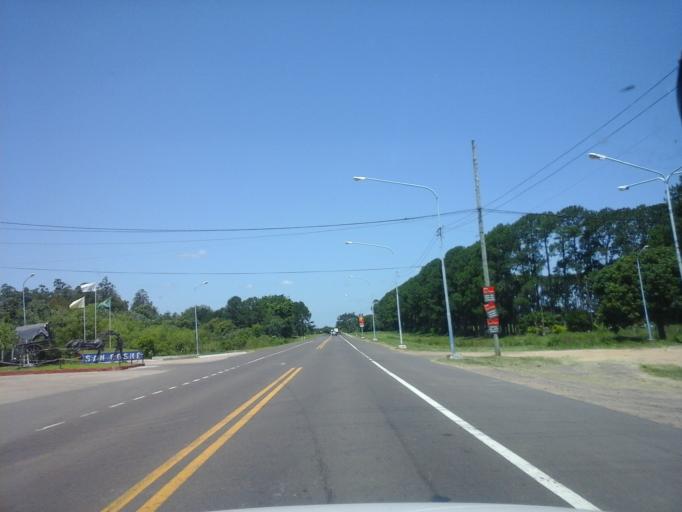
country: AR
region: Corrientes
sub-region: Departamento de San Cosme
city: San Cosme
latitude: -27.3733
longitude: -58.4872
